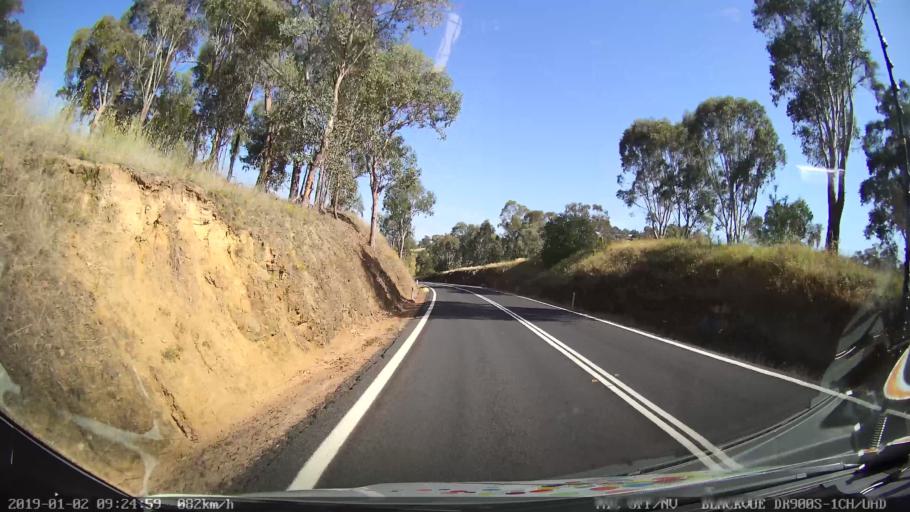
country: AU
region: New South Wales
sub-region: Tumut Shire
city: Tumut
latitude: -35.3698
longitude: 148.2918
